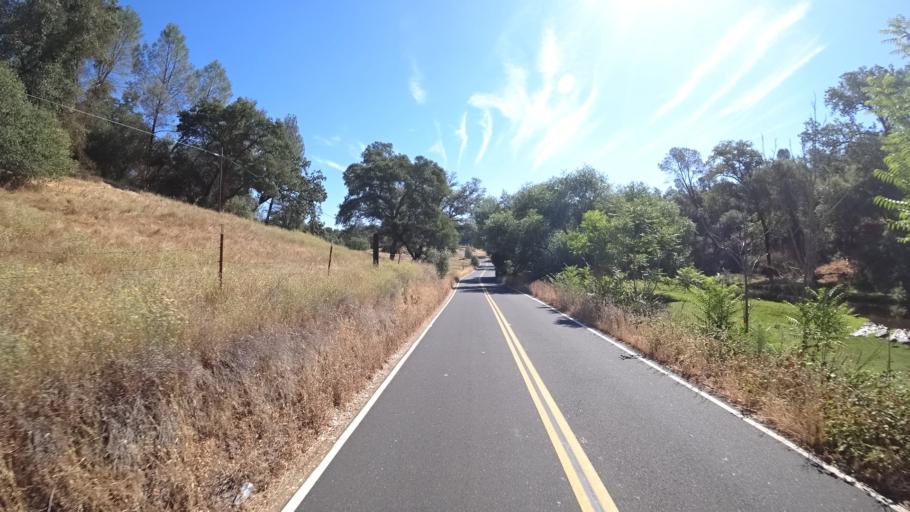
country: US
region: California
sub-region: Calaveras County
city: San Andreas
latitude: 38.1349
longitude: -120.6300
